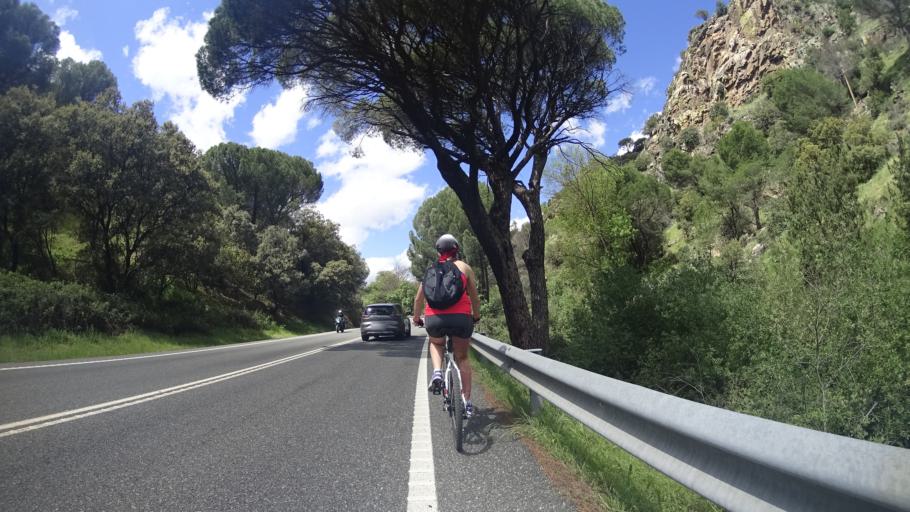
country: ES
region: Madrid
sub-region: Provincia de Madrid
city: Pelayos de la Presa
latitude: 40.3667
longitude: -4.3083
